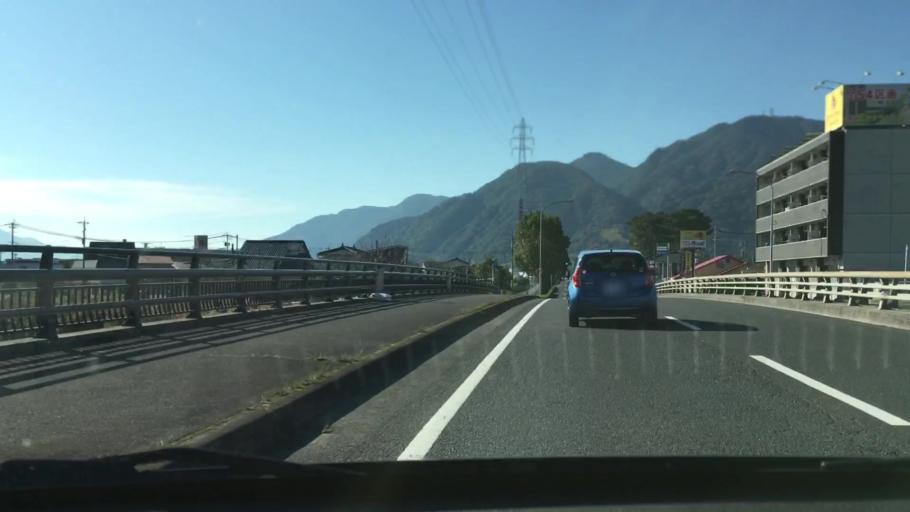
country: JP
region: Kagoshima
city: Kajiki
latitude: 31.7167
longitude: 130.6193
